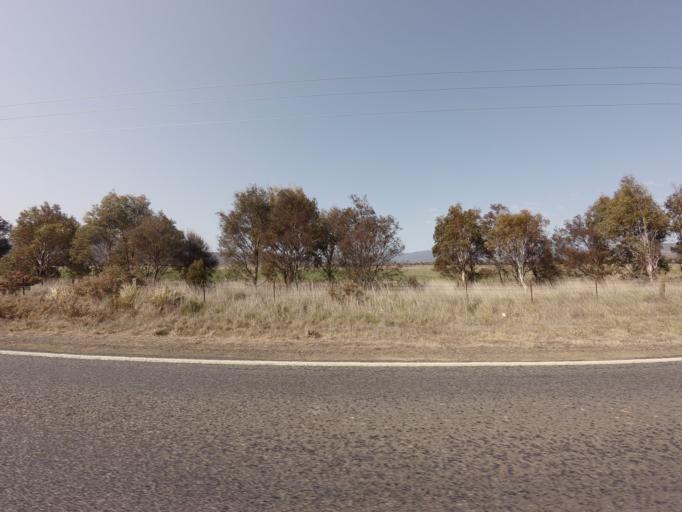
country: AU
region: Tasmania
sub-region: Northern Midlands
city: Evandale
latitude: -41.7911
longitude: 147.7116
